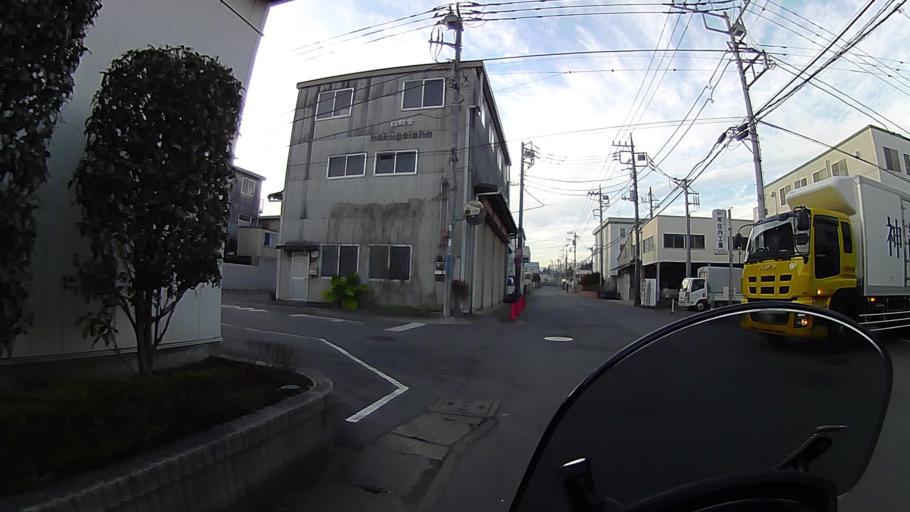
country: JP
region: Kanagawa
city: Atsugi
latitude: 35.4247
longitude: 139.4211
